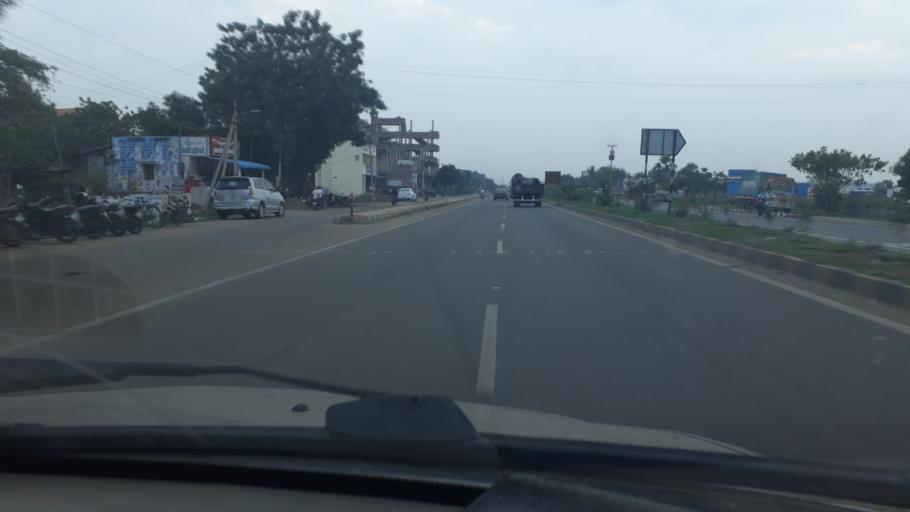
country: IN
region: Tamil Nadu
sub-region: Thoothukkudi
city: Korampallam
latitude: 8.7822
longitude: 78.1007
